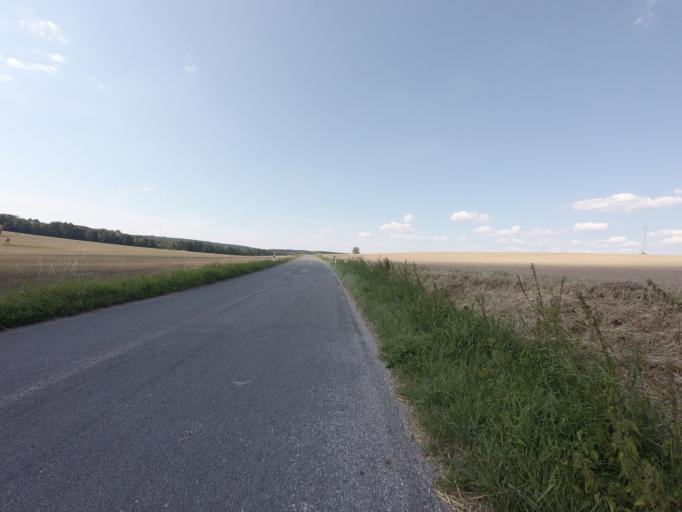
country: CZ
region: Jihocesky
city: Tyn nad Vltavou
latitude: 49.1432
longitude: 14.4470
